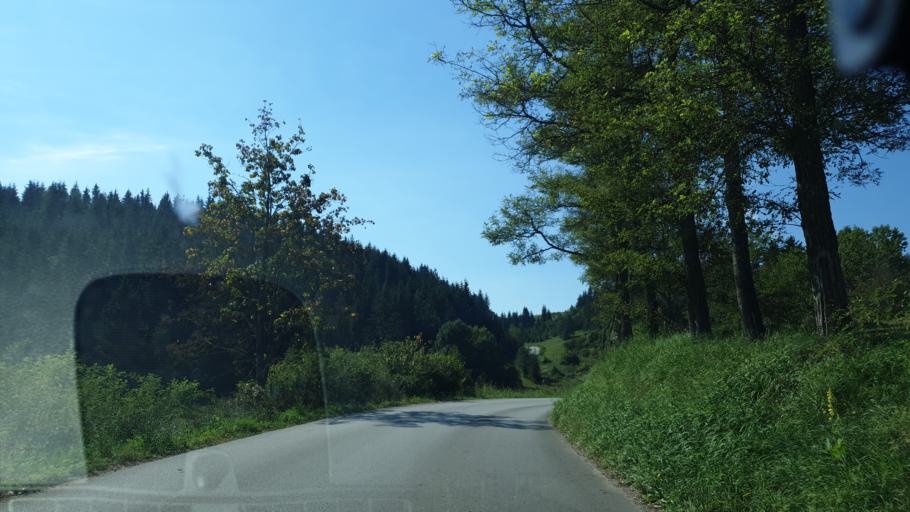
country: RS
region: Central Serbia
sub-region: Zlatiborski Okrug
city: Nova Varos
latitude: 43.4330
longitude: 19.8740
